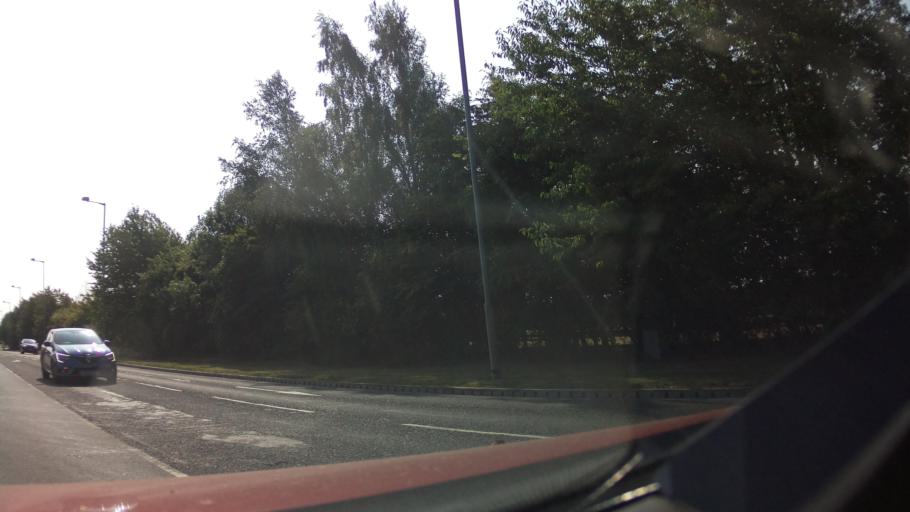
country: GB
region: England
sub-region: Staffordshire
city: Lichfield
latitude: 52.6752
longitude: -1.8496
